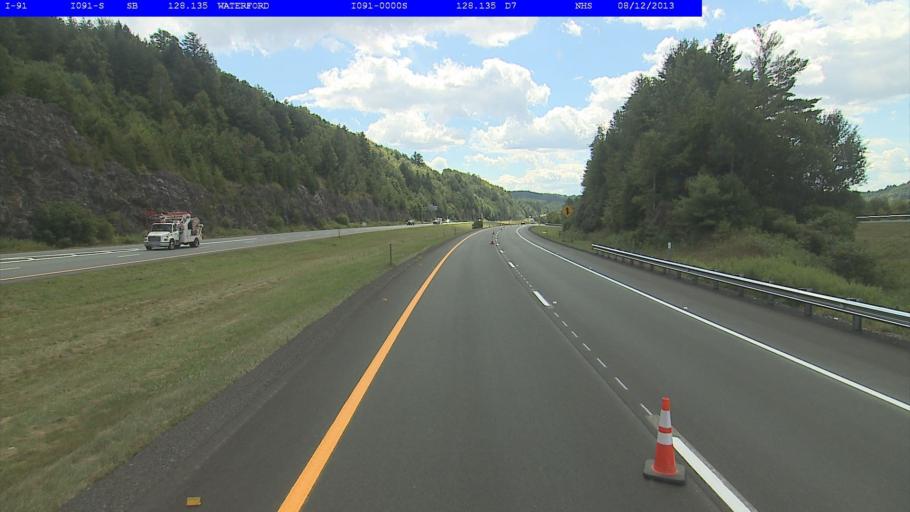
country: US
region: Vermont
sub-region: Caledonia County
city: Saint Johnsbury
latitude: 44.3948
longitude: -72.0175
